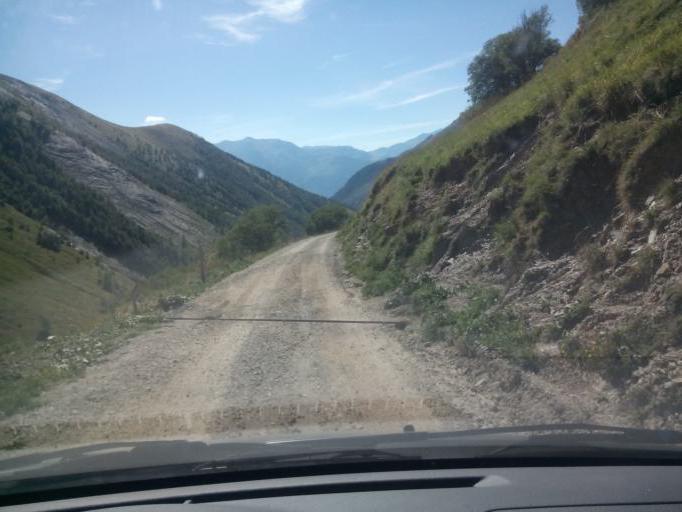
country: FR
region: Rhone-Alpes
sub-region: Departement de l'Isere
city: Mont-de-Lans
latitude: 45.0724
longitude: 6.1864
